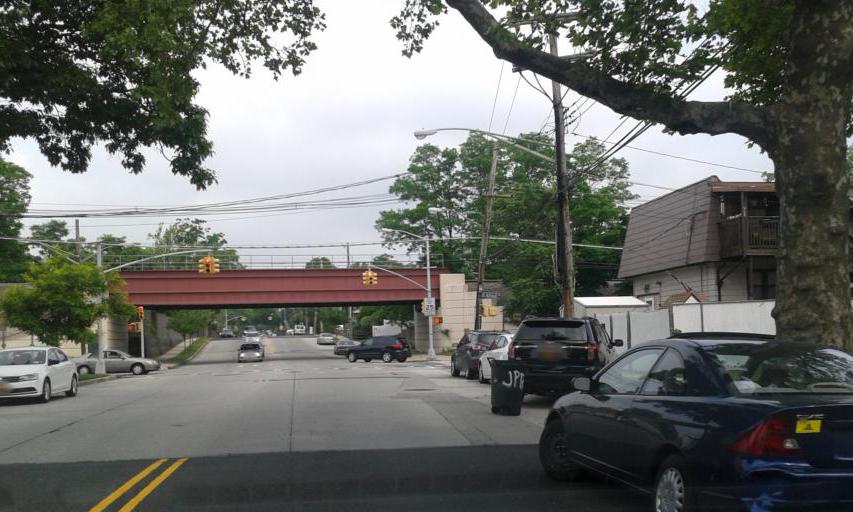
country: US
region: New York
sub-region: Richmond County
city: Staten Island
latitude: 40.5676
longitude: -74.1226
